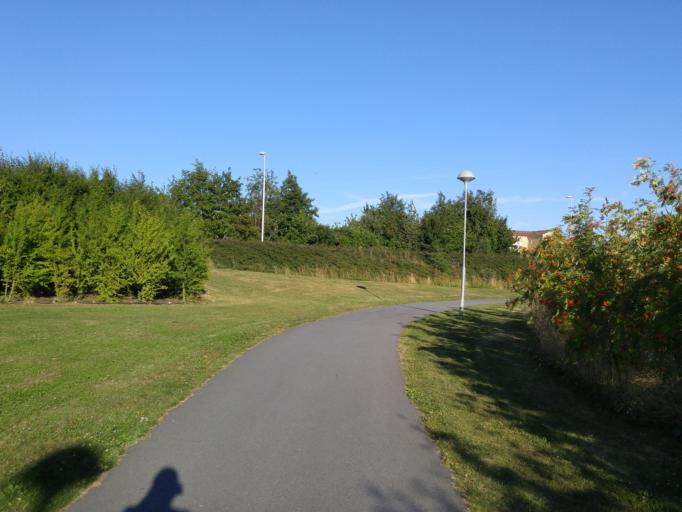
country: SE
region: Skane
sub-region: Lunds Kommun
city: Lund
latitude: 55.7314
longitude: 13.2000
